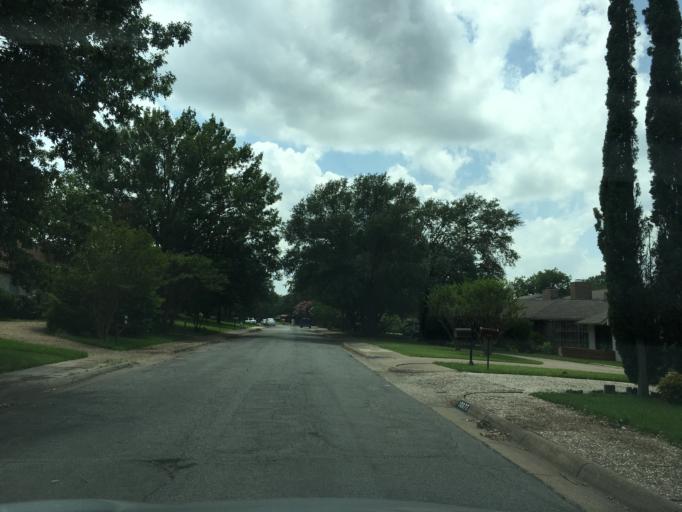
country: US
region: Texas
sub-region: Dallas County
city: University Park
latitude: 32.8923
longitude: -96.7794
